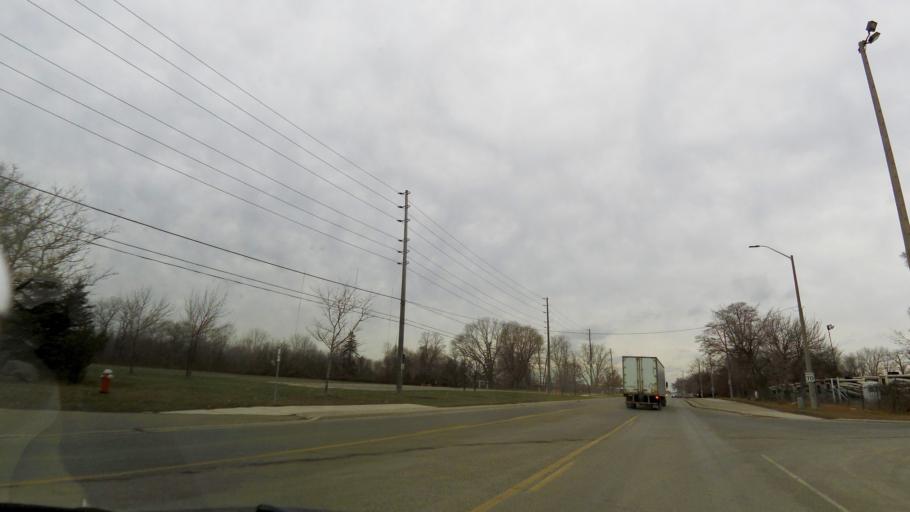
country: CA
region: Ontario
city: Oakville
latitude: 43.5040
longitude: -79.6205
